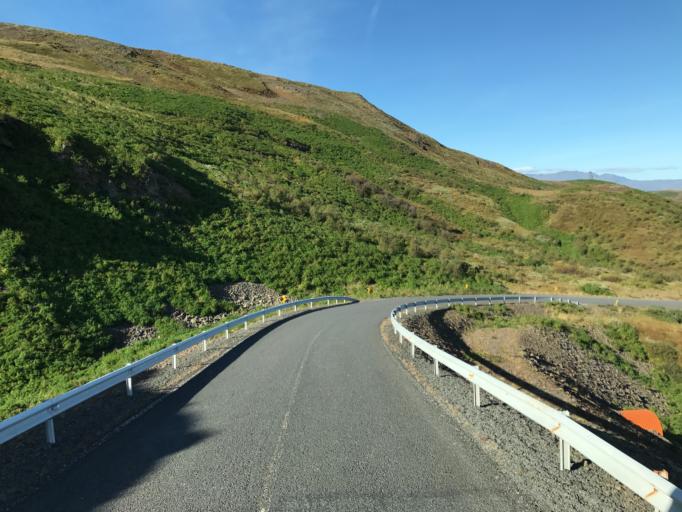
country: IS
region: South
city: Hveragerdi
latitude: 64.1189
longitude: -21.2614
